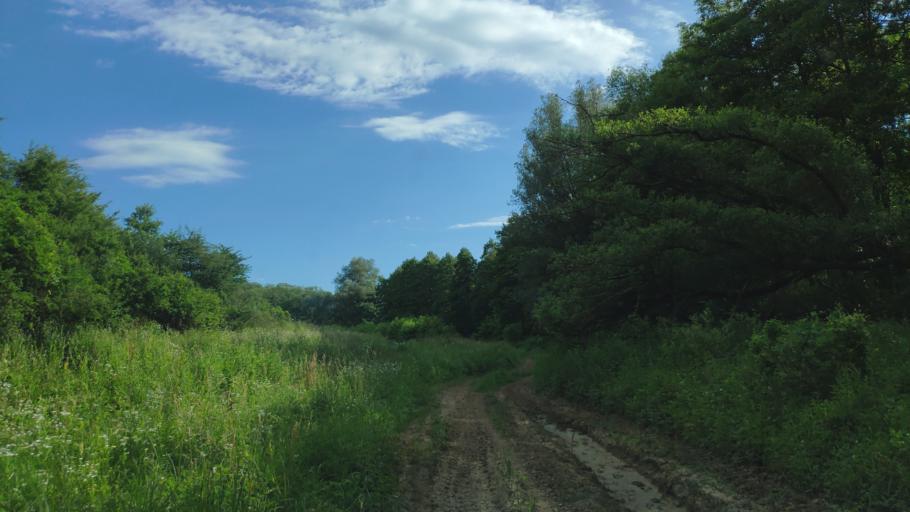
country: SK
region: Banskobystricky
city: Rimavska Sobota
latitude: 48.2564
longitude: 20.1084
